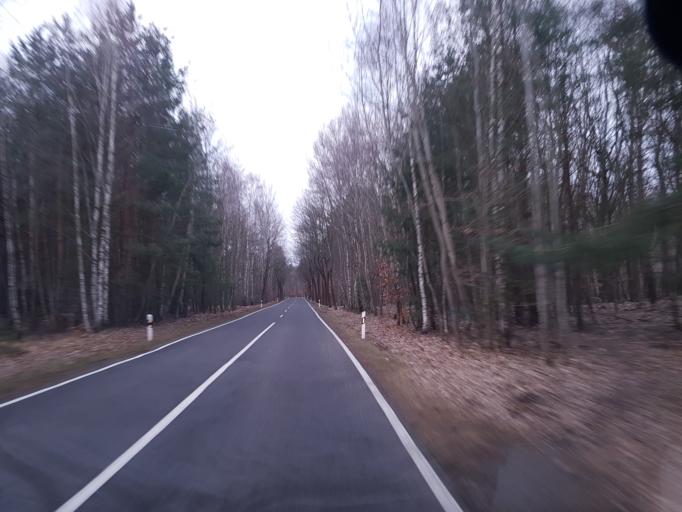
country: DE
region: Brandenburg
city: Sallgast
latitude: 51.5767
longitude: 13.8519
